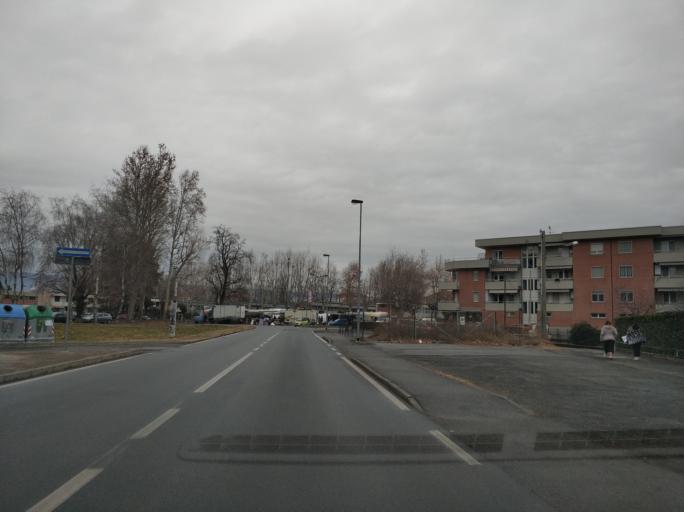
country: IT
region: Piedmont
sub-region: Provincia di Torino
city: Ivrea
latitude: 45.4482
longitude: 7.8756
